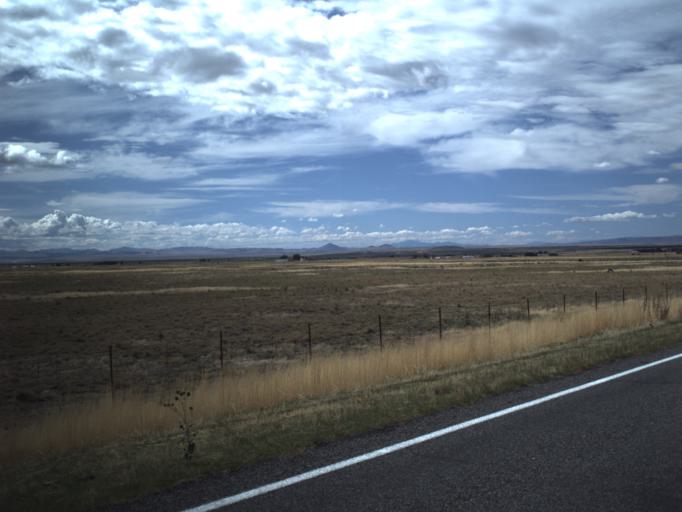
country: US
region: Utah
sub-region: Millard County
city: Fillmore
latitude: 38.9791
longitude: -112.3775
